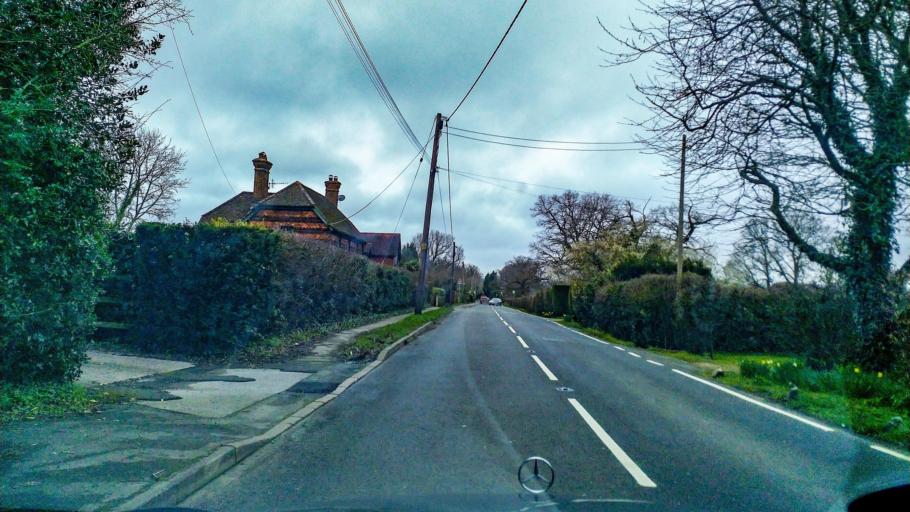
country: GB
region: England
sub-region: Surrey
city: Reigate
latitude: 51.2084
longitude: -0.2507
